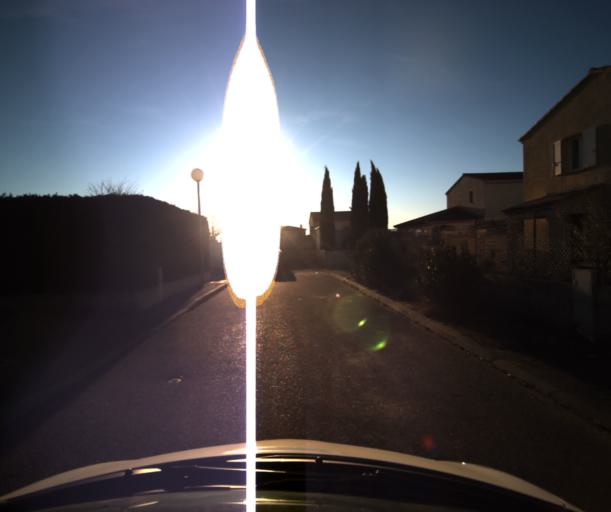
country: FR
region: Provence-Alpes-Cote d'Azur
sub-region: Departement du Vaucluse
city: Pertuis
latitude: 43.7076
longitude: 5.5063
